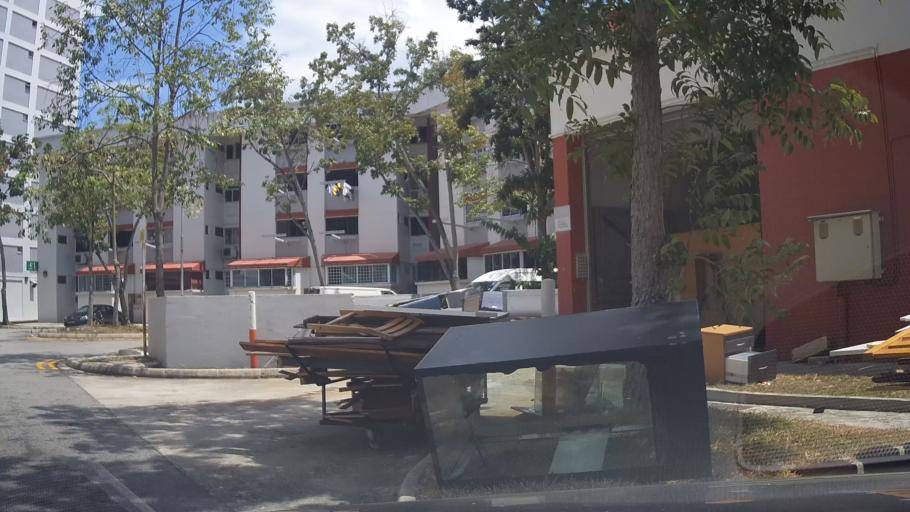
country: SG
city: Singapore
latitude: 1.3591
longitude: 103.9467
